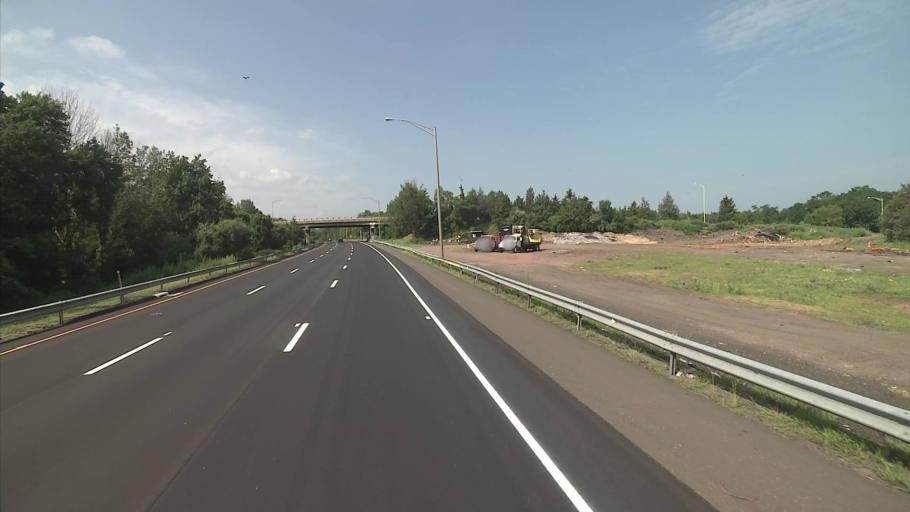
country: US
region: Connecticut
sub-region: New Haven County
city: Wallingford Center
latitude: 41.4240
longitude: -72.8237
